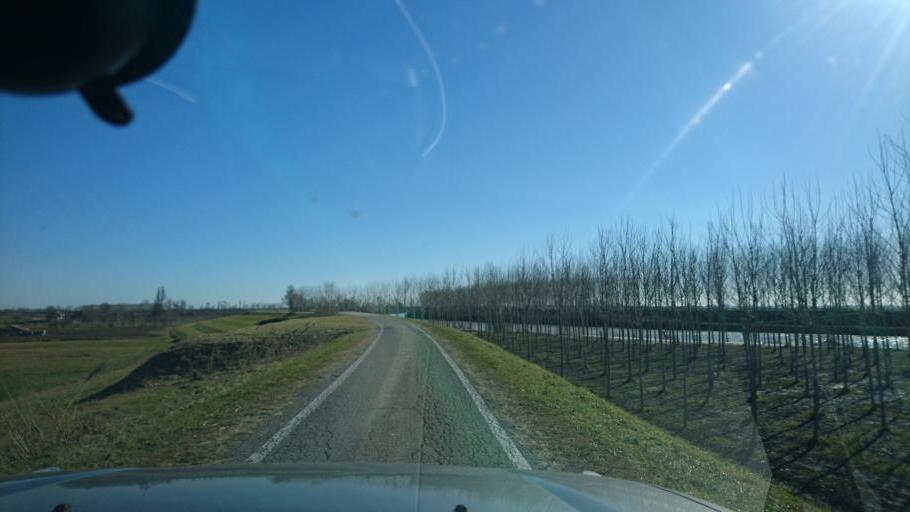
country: IT
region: Veneto
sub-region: Provincia di Rovigo
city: Ariano
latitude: 44.9341
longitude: 12.1320
